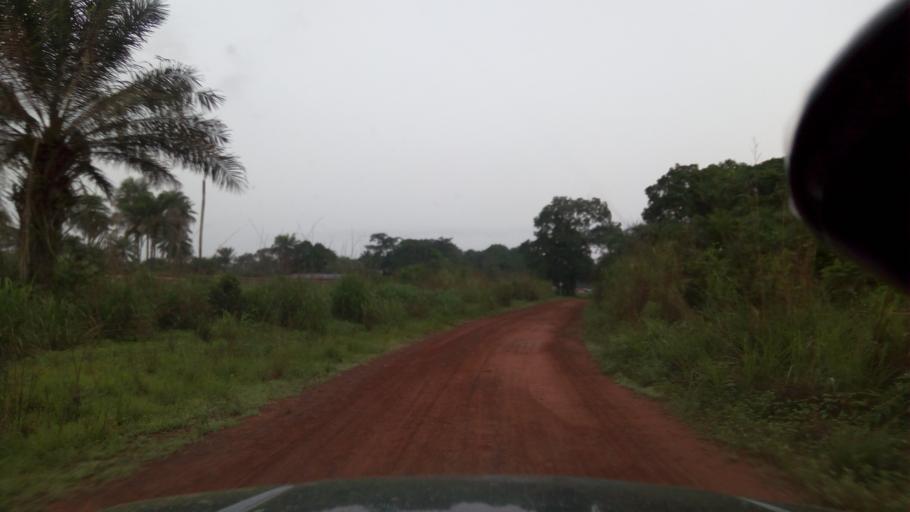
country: SL
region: Northern Province
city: Port Loko
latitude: 8.7209
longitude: -12.7979
